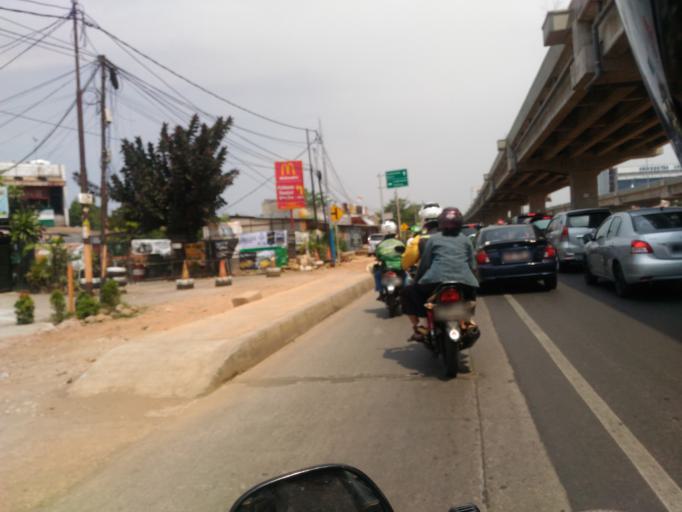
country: ID
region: Jakarta Raya
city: Jakarta
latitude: -6.2410
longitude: 106.8956
